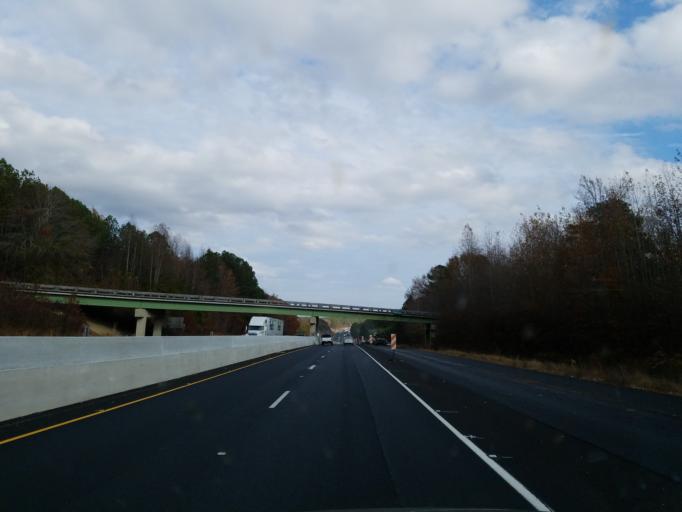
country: US
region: Georgia
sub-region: Haralson County
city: Tallapoosa
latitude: 33.6706
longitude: -85.3593
